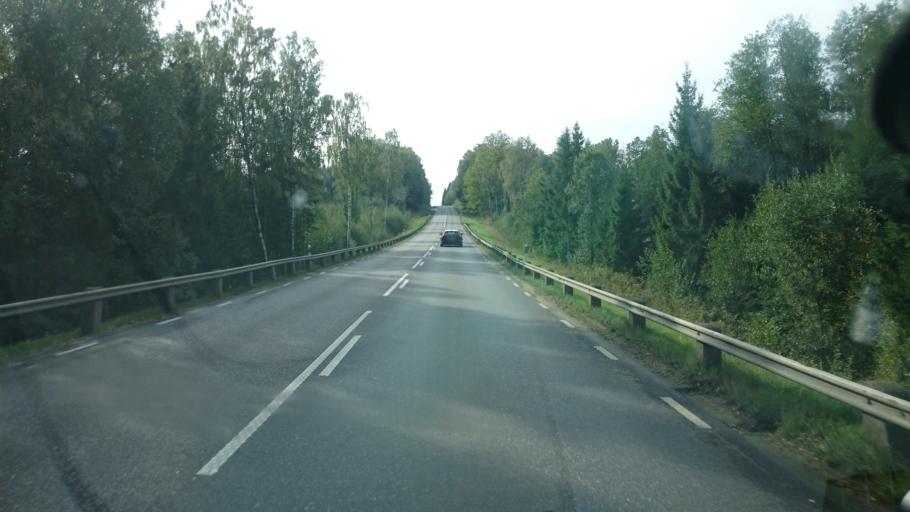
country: SE
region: Vaestra Goetaland
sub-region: Alingsas Kommun
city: Sollebrunn
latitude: 58.0328
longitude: 12.4643
